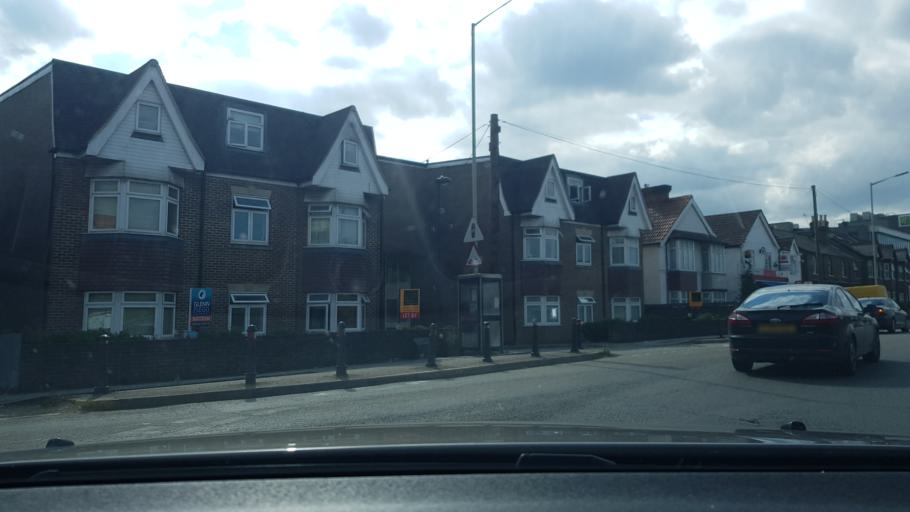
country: GB
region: England
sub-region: Surrey
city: Colnbrook
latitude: 51.4884
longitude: -0.5339
